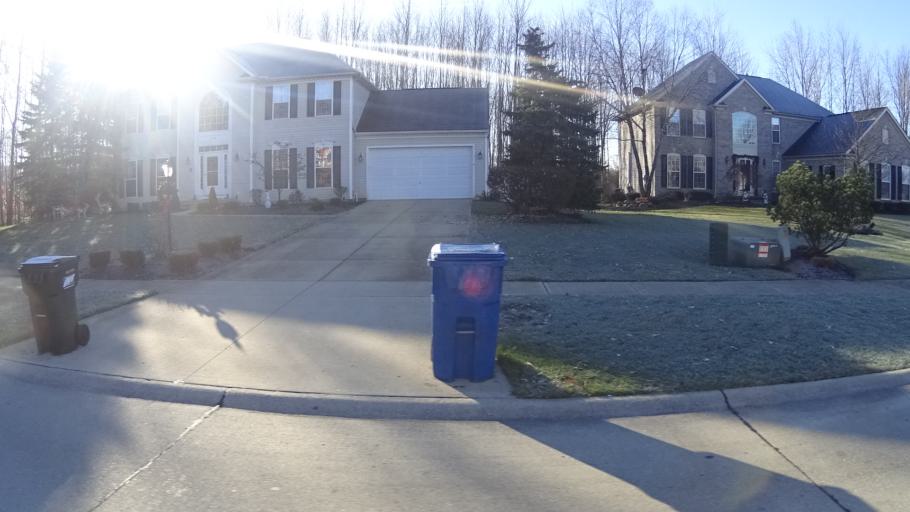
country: US
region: Ohio
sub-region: Lorain County
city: Sheffield Lake
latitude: 41.4567
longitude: -82.0768
